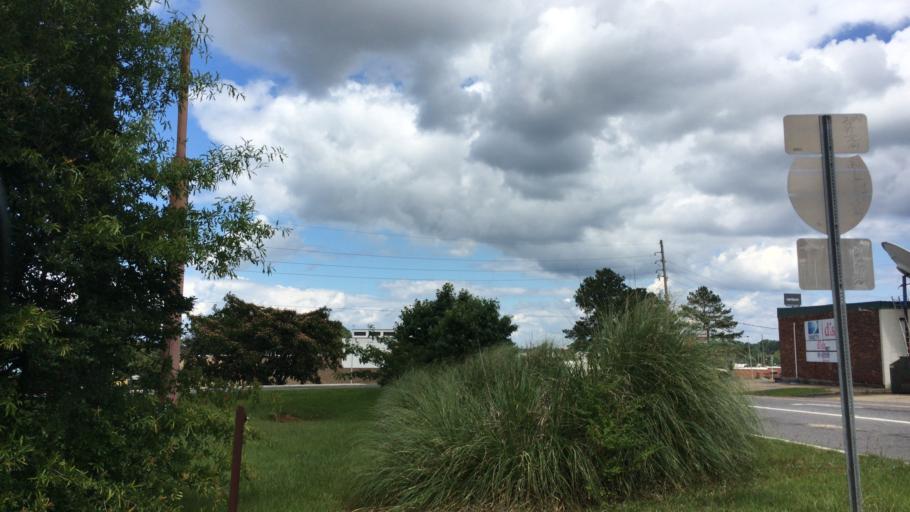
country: US
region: Louisiana
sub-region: Lincoln Parish
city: Ruston
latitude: 32.5426
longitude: -92.6395
